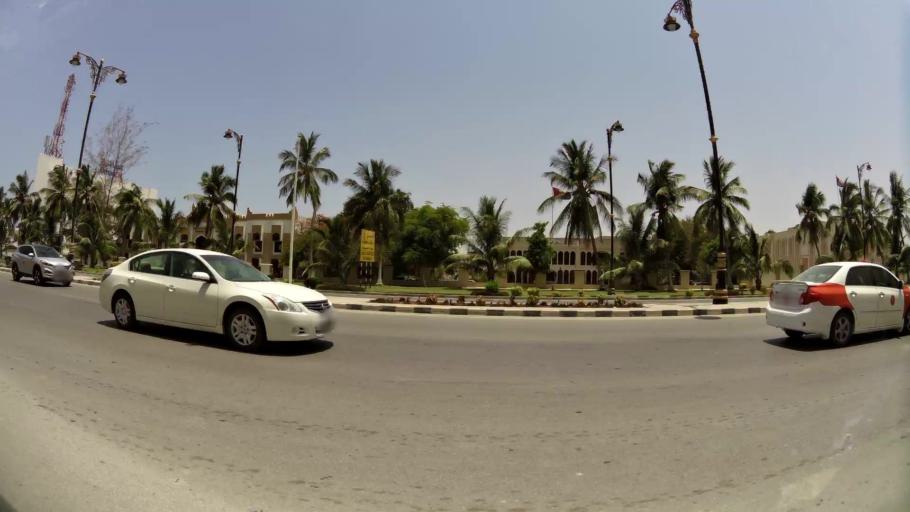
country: OM
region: Zufar
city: Salalah
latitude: 17.0215
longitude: 54.0919
